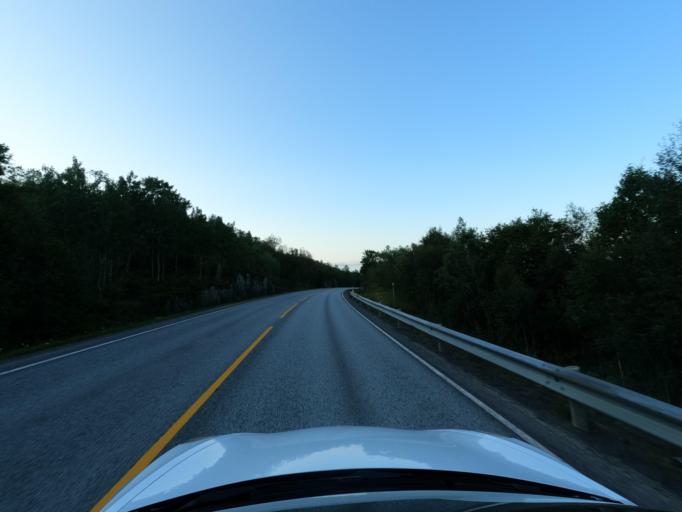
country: NO
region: Troms
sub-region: Harstad
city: Harstad
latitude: 68.7373
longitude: 16.5544
